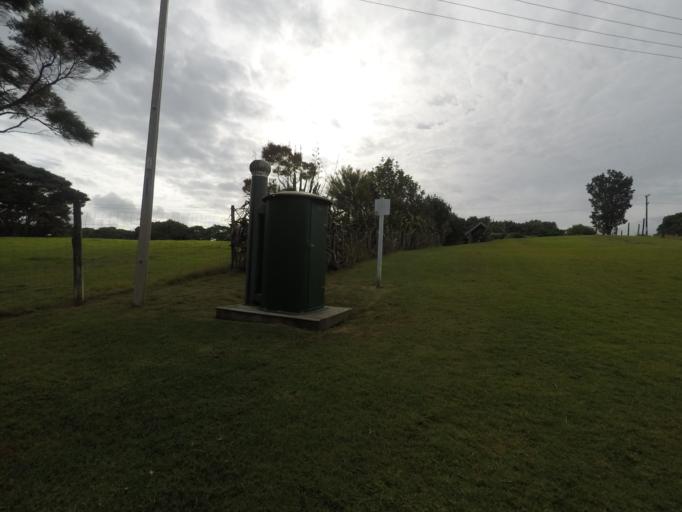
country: NZ
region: Auckland
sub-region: Auckland
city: Parakai
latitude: -36.5157
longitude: 174.2436
